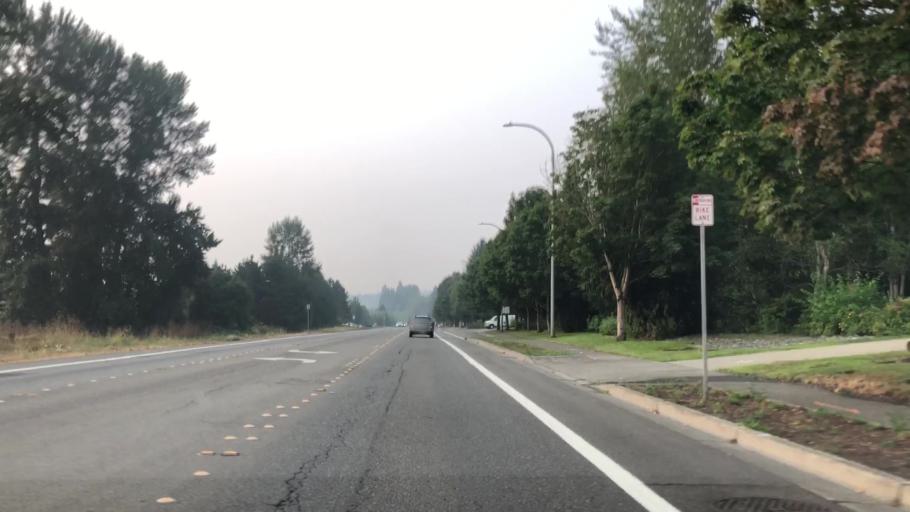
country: US
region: Washington
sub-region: King County
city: Redmond
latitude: 47.6966
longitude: -122.1519
